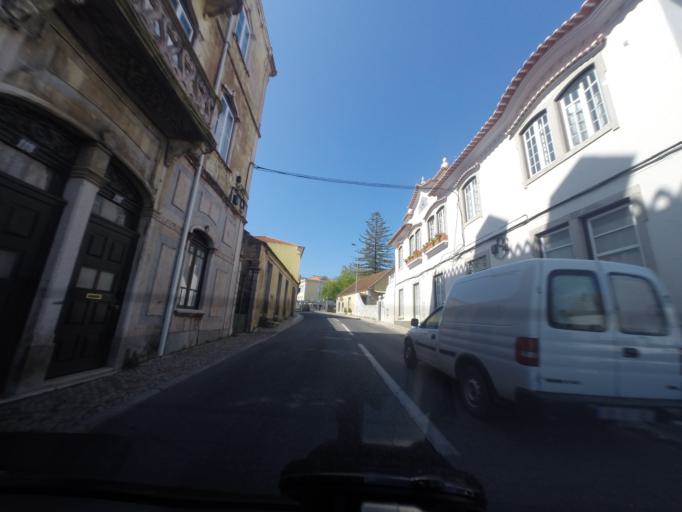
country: PT
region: Lisbon
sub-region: Sintra
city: Sintra
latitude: 38.8044
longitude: -9.3810
